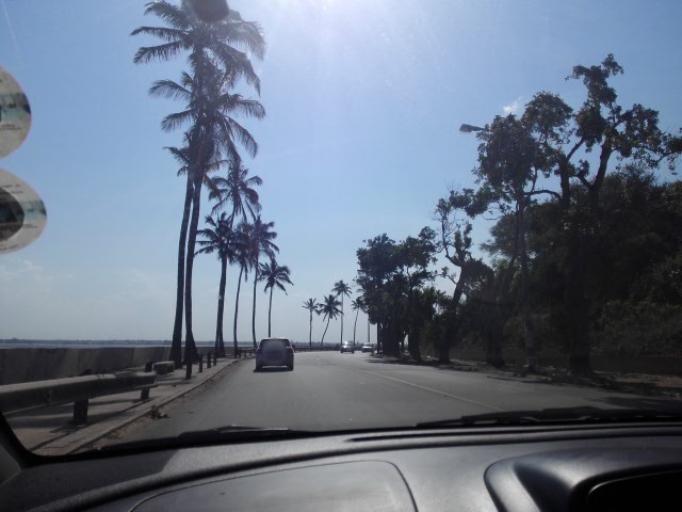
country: MZ
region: Maputo City
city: Maputo
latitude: -25.9839
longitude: 32.5904
